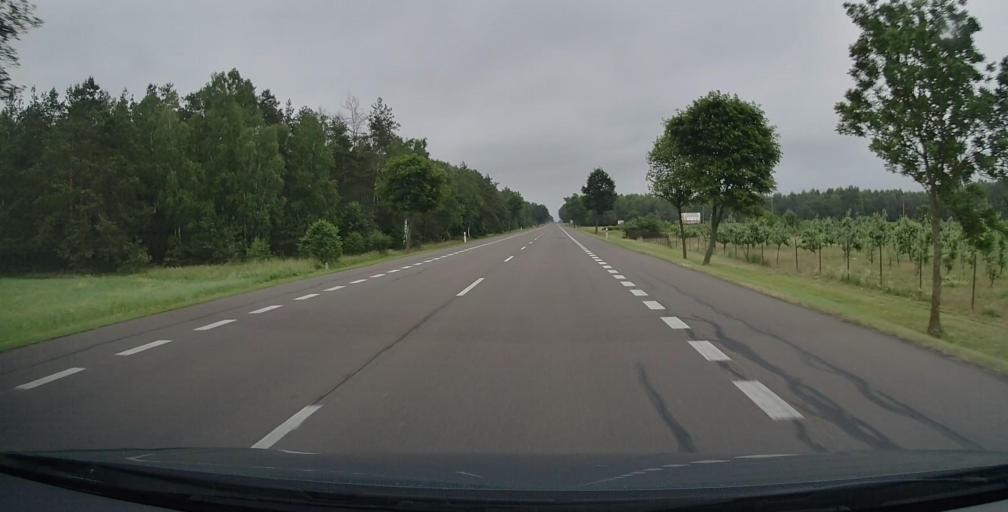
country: PL
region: Lublin Voivodeship
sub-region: Powiat bialski
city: Lesna Podlaska
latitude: 52.0368
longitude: 22.9905
